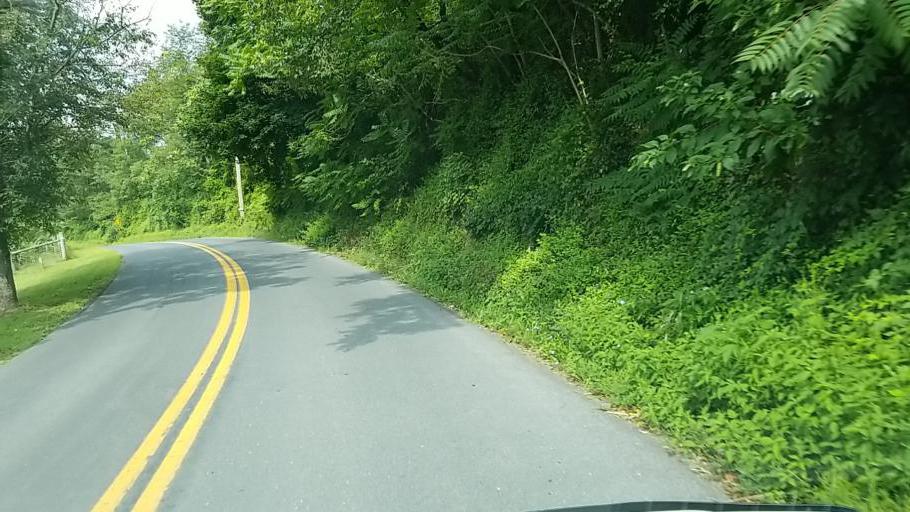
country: US
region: Pennsylvania
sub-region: Dauphin County
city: Millersburg
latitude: 40.5108
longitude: -76.9076
